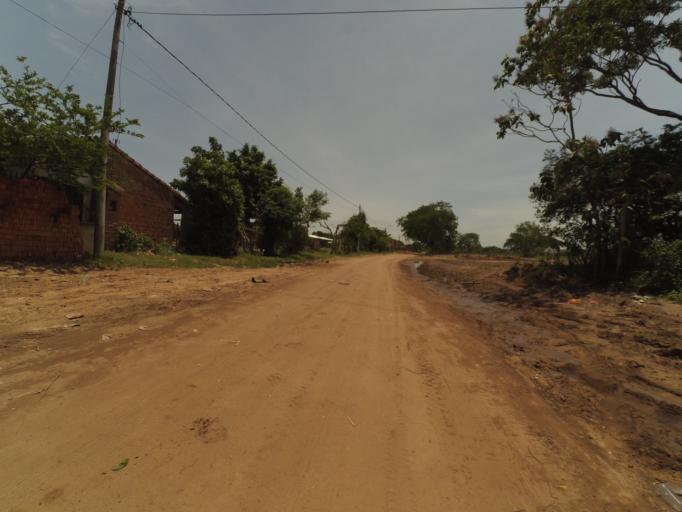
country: BO
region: Santa Cruz
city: Santa Cruz de la Sierra
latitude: -17.8241
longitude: -63.2529
